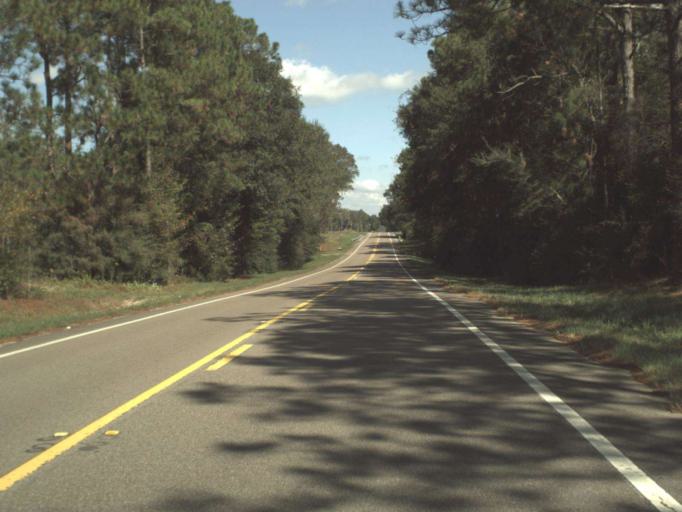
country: US
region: Alabama
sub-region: Geneva County
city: Samson
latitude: 30.9373
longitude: -86.1373
